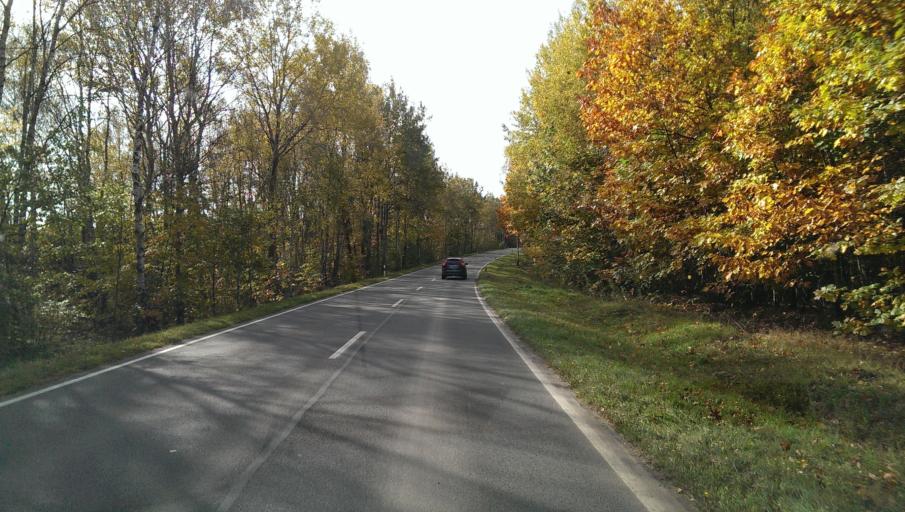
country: DE
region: Brandenburg
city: Lauchhammer
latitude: 51.5238
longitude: 13.7139
